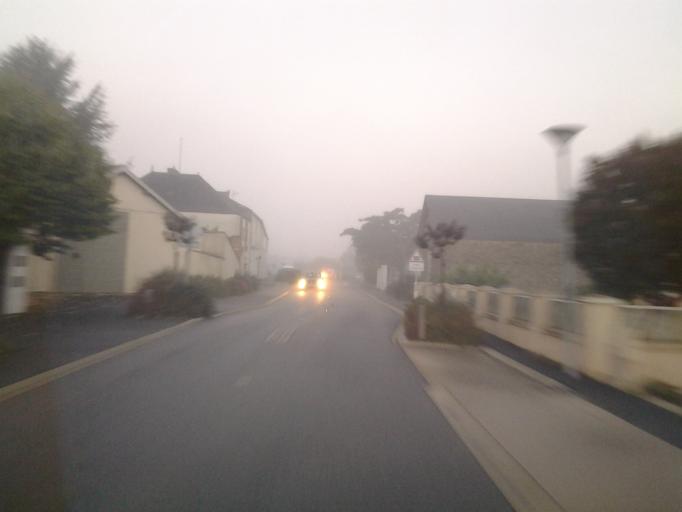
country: FR
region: Pays de la Loire
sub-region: Departement de la Vendee
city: Nesmy
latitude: 46.5948
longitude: -1.4092
